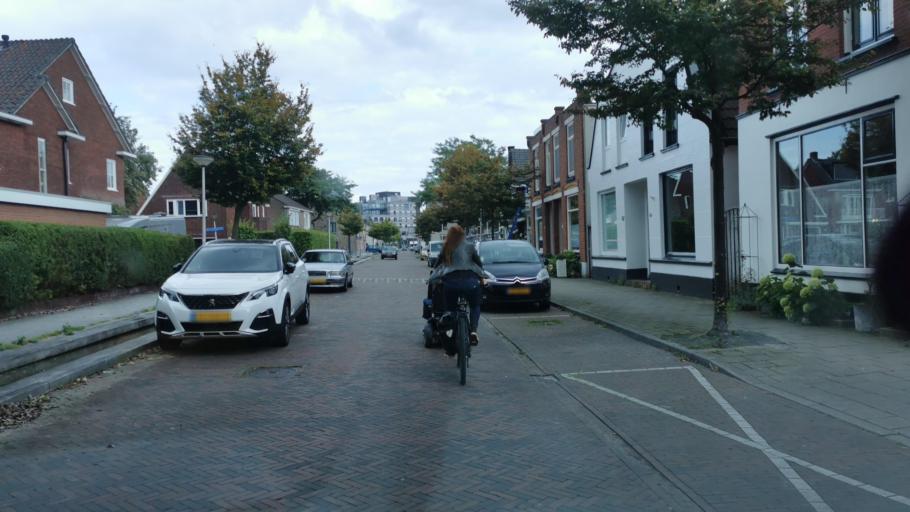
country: NL
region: Overijssel
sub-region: Gemeente Enschede
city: Enschede
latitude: 52.2287
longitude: 6.8860
